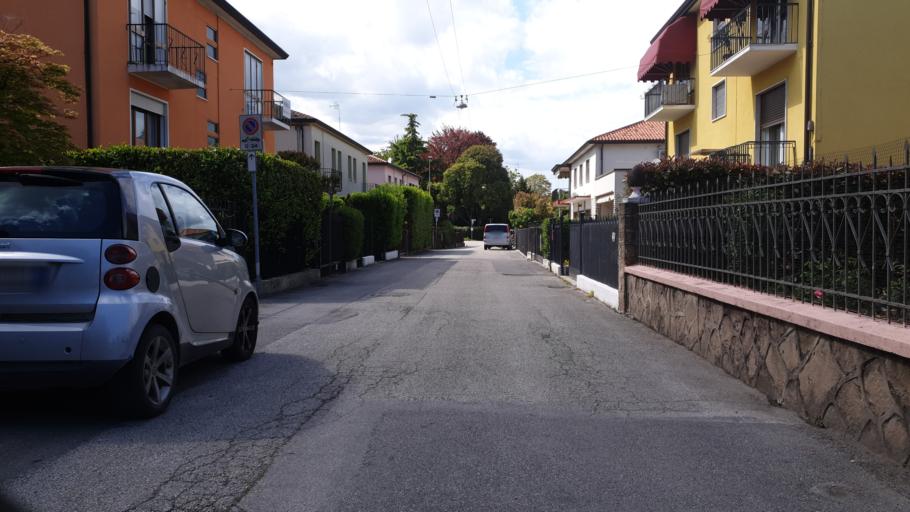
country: IT
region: Veneto
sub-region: Provincia di Padova
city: Noventa
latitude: 45.4220
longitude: 11.9405
